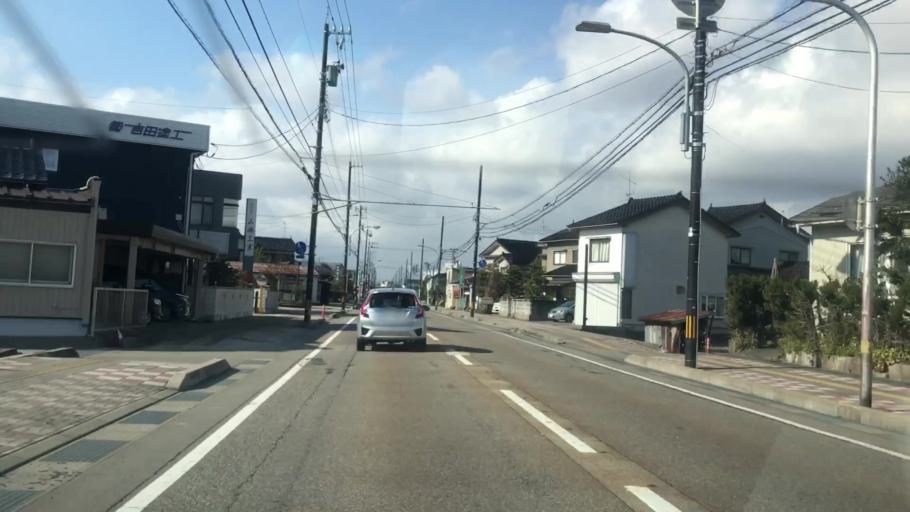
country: JP
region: Toyama
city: Takaoka
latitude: 36.7286
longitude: 137.0589
